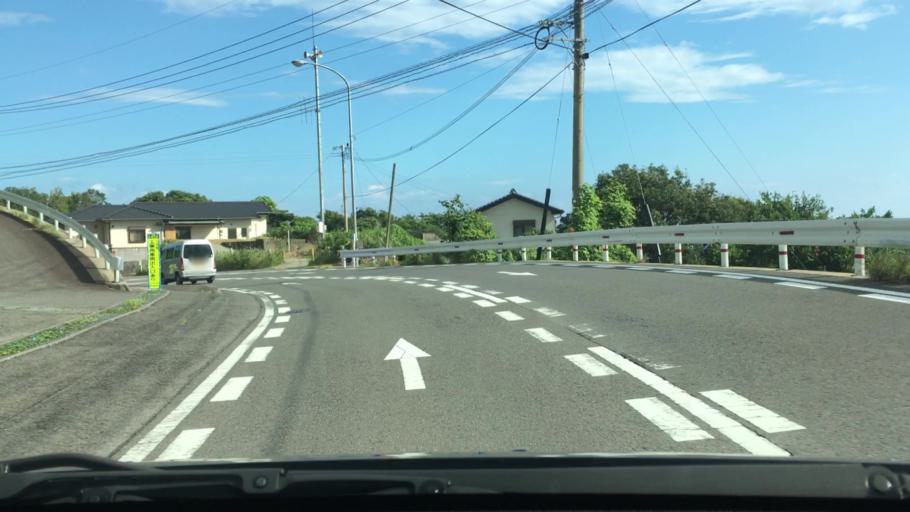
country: JP
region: Nagasaki
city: Togitsu
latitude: 32.8544
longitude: 129.6867
